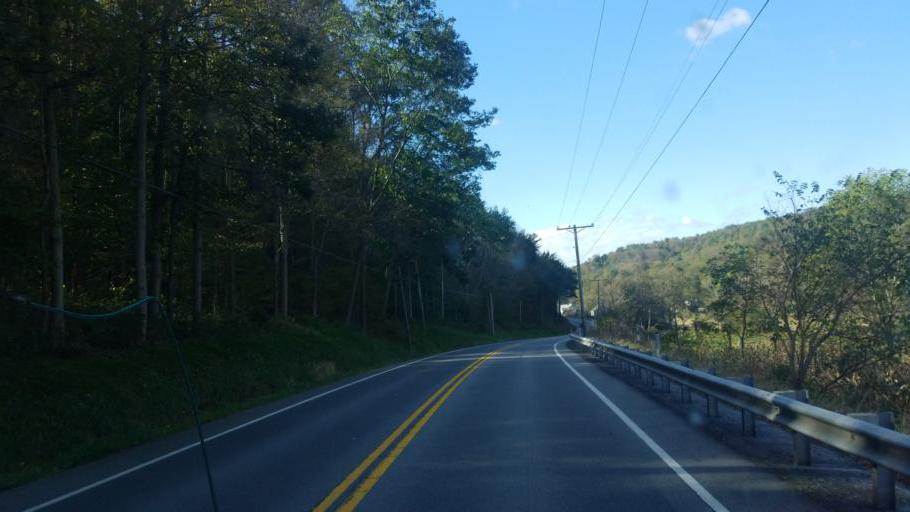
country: US
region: Pennsylvania
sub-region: Blair County
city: Claysburg
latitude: 40.1804
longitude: -78.5067
